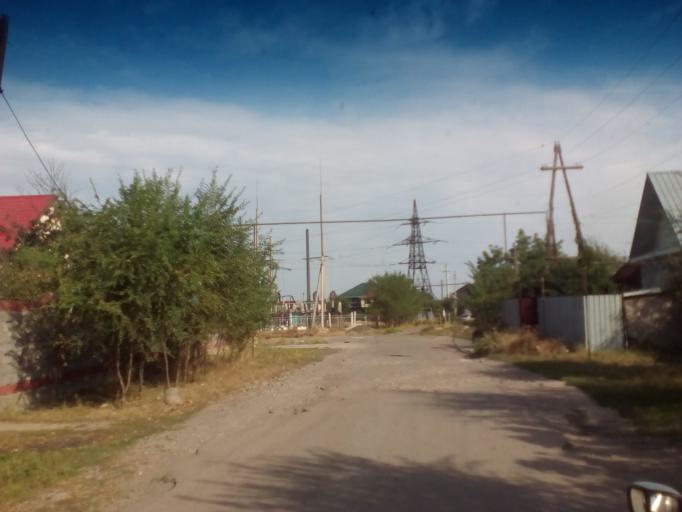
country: KZ
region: Almaty Oblysy
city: Burunday
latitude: 43.1690
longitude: 76.4029
